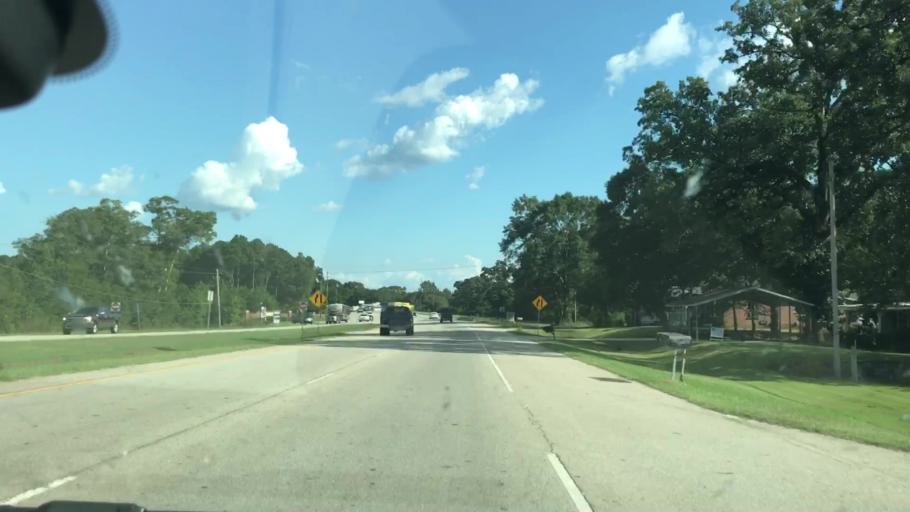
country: US
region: Georgia
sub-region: Troup County
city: La Grange
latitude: 32.9971
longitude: -85.0101
